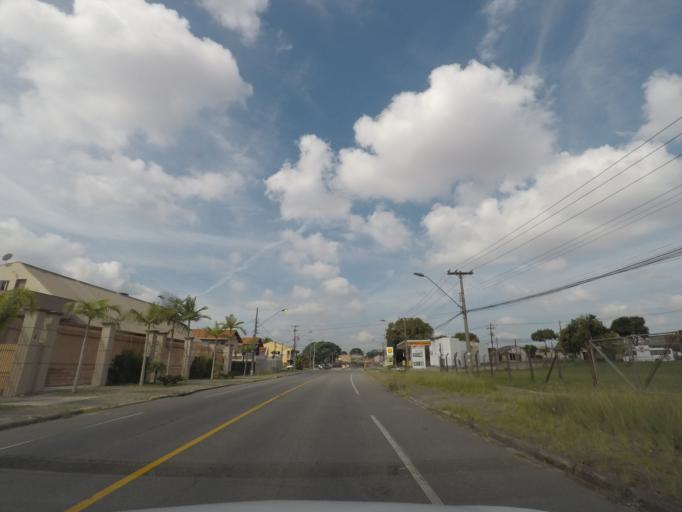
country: BR
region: Parana
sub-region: Pinhais
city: Pinhais
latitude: -25.4461
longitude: -49.2187
